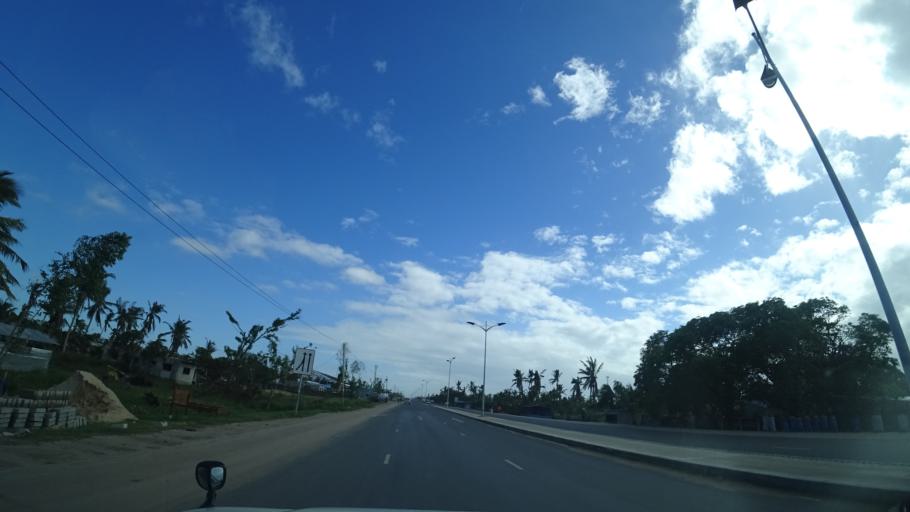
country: MZ
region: Sofala
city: Beira
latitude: -19.7698
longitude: 34.8827
